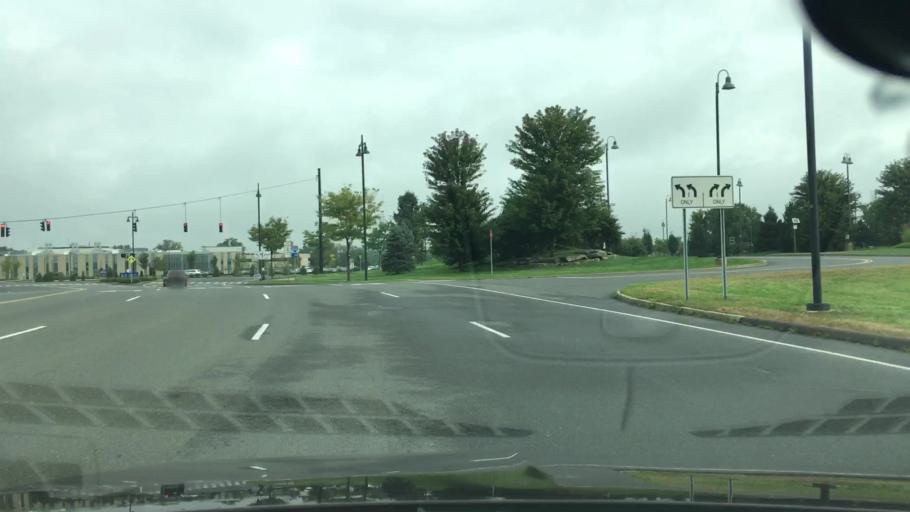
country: US
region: Connecticut
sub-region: Hartford County
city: East Hartford
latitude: 41.7547
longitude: -72.6241
